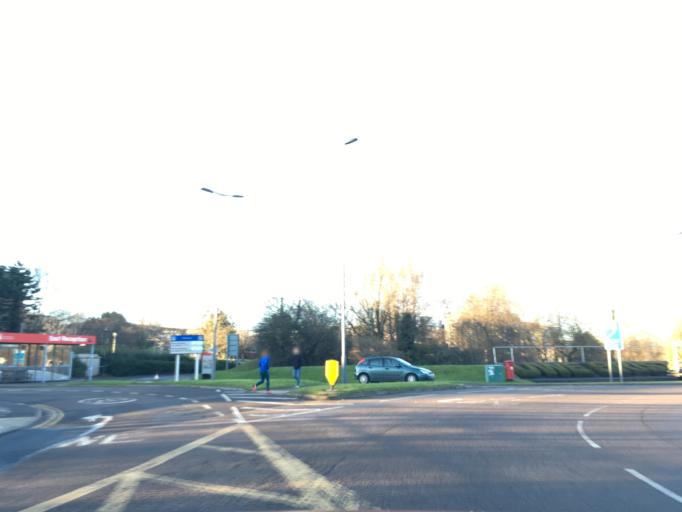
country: GB
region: England
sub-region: South Gloucestershire
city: Stoke Gifford
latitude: 51.4999
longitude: -2.5444
